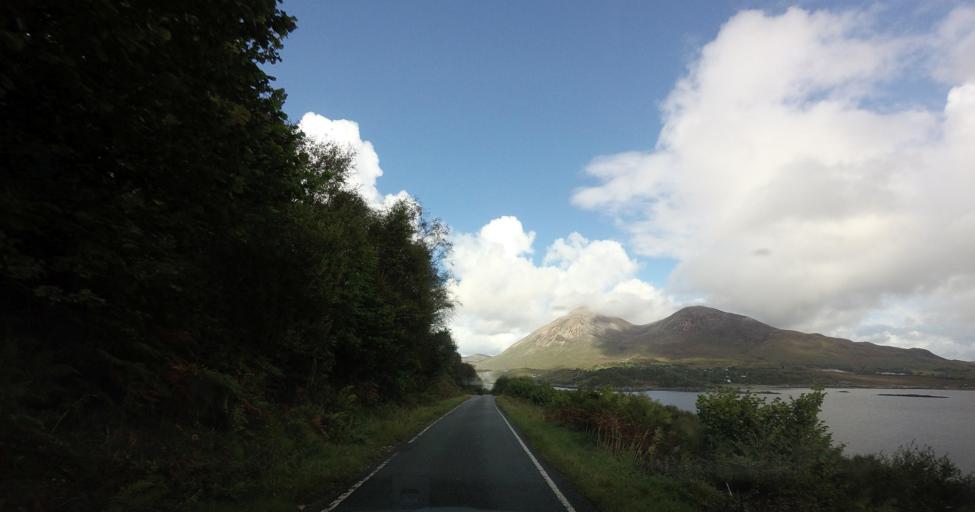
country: GB
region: Scotland
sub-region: Highland
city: Portree
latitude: 57.1978
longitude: -6.0277
